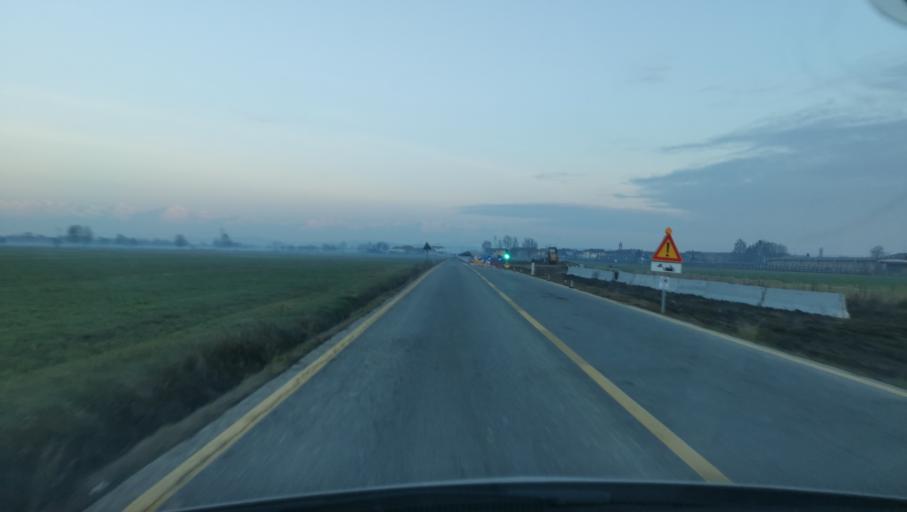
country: IT
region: Piedmont
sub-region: Provincia di Torino
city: Montanaro
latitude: 45.2483
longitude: 7.8916
